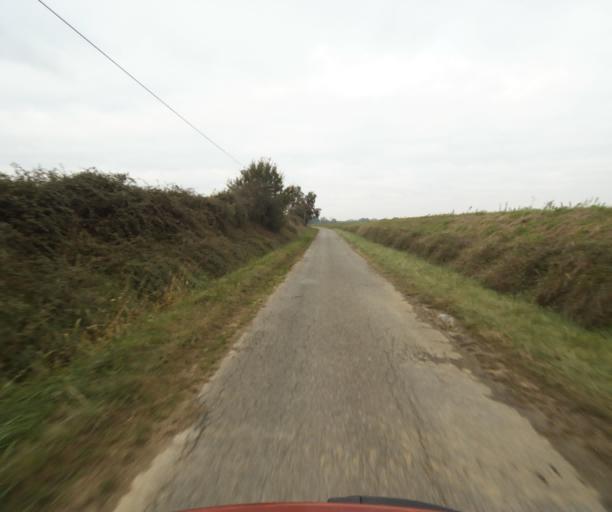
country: FR
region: Midi-Pyrenees
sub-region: Departement du Tarn-et-Garonne
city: Verdun-sur-Garonne
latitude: 43.8100
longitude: 1.2104
